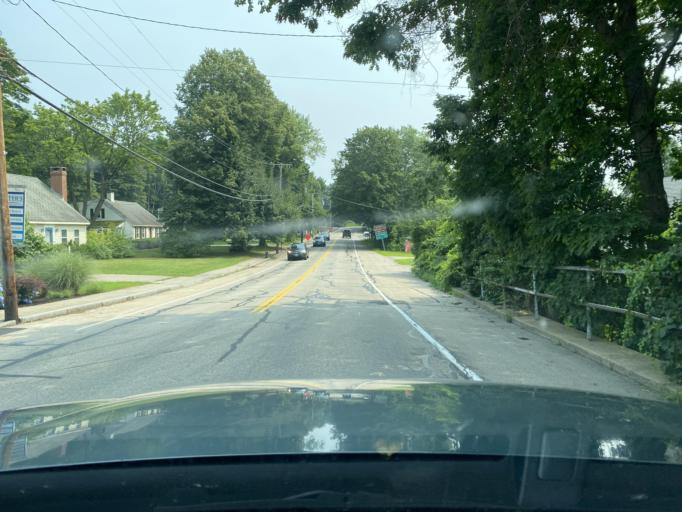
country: US
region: Maine
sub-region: York County
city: York Harbor
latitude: 43.1398
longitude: -70.6464
